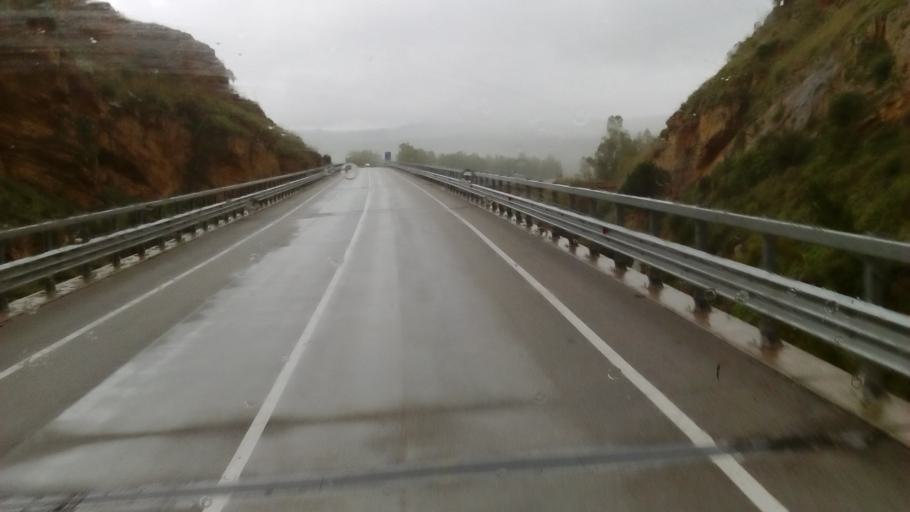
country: IT
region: Sicily
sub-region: Enna
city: Pietraperzia
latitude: 37.4976
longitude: 14.1432
